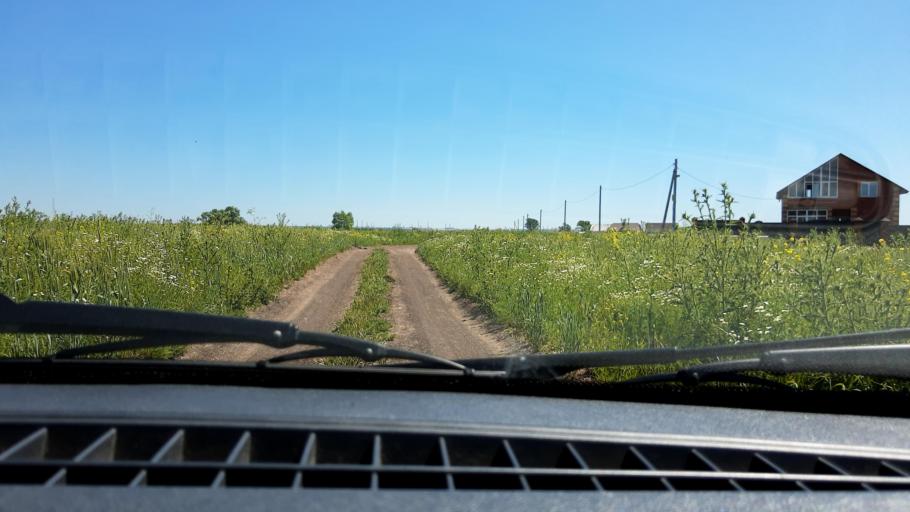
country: RU
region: Bashkortostan
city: Mikhaylovka
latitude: 54.8751
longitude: 55.9329
